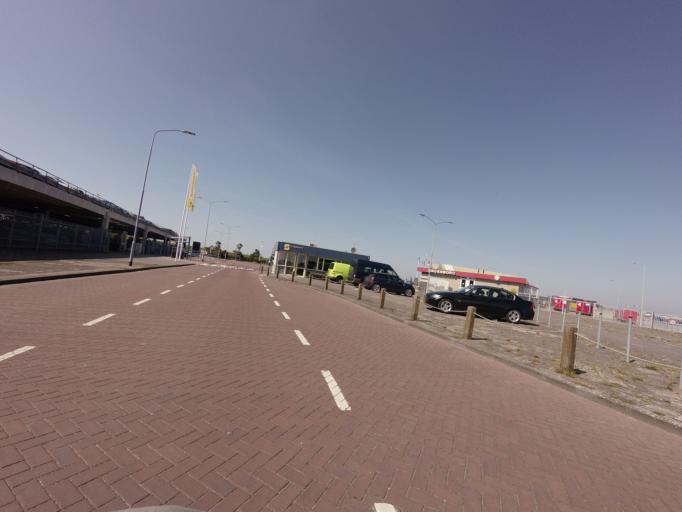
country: NL
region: Friesland
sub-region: Gemeente Dongeradeel
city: Anjum
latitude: 53.4097
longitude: 6.1969
